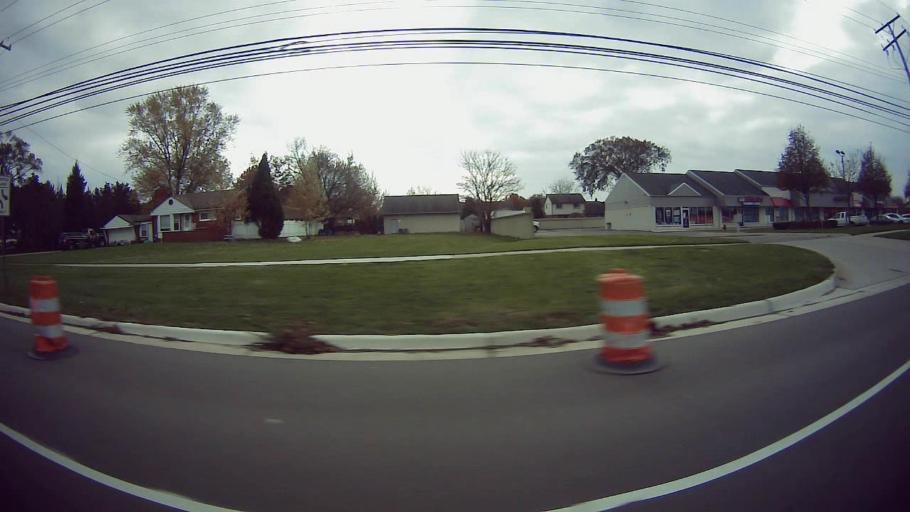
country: US
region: Michigan
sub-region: Macomb County
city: Fraser
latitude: 42.5527
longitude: -82.9779
